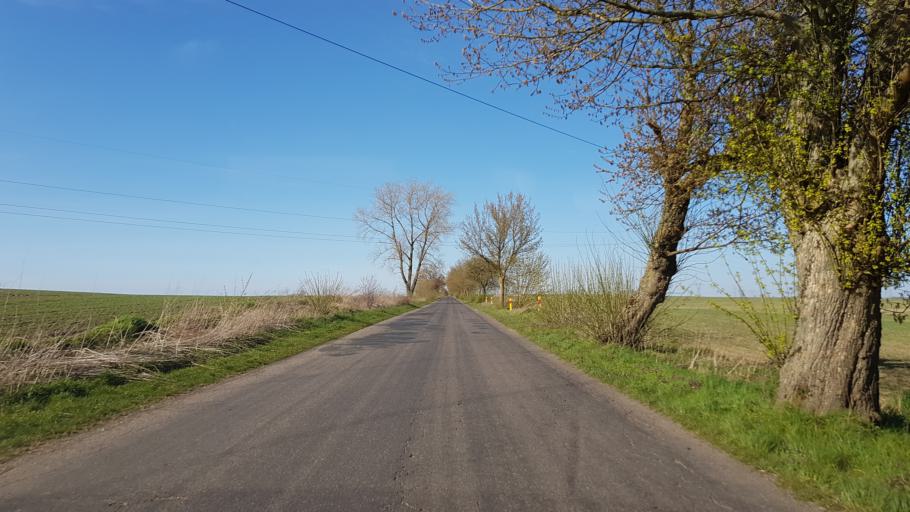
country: PL
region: West Pomeranian Voivodeship
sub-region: Powiat stargardzki
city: Stargard Szczecinski
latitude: 53.3766
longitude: 15.0332
